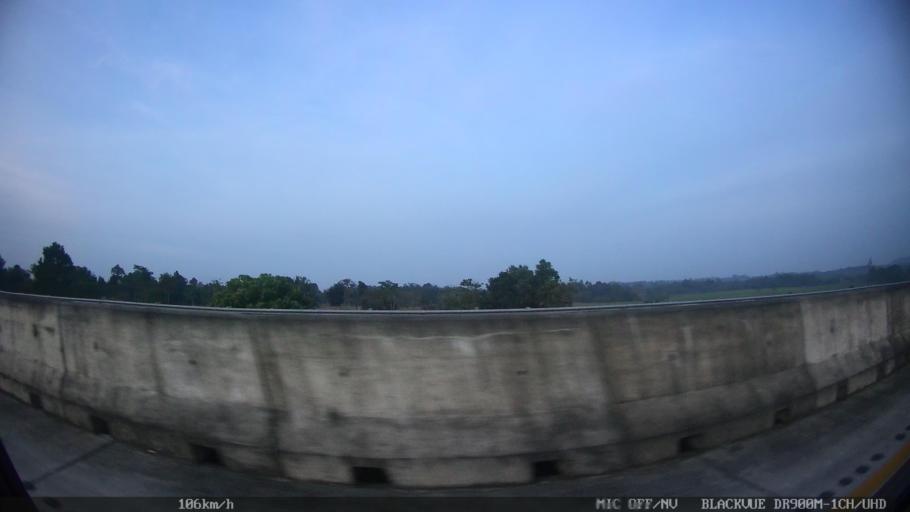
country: ID
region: Lampung
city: Penengahan
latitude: -5.7530
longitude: 105.7085
